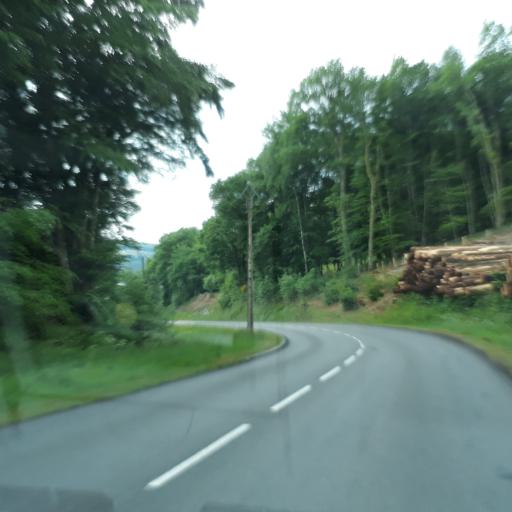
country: FR
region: Limousin
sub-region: Departement de la Haute-Vienne
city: Eymoutiers
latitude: 45.7548
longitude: 1.7440
